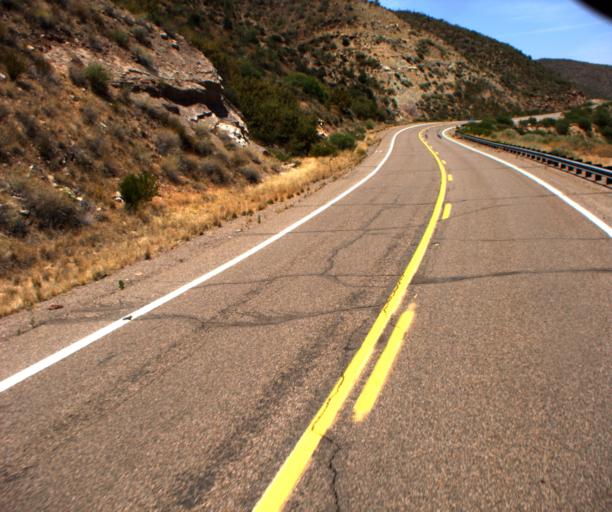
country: US
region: Arizona
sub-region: Gila County
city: Tonto Basin
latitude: 33.6781
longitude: -111.1620
